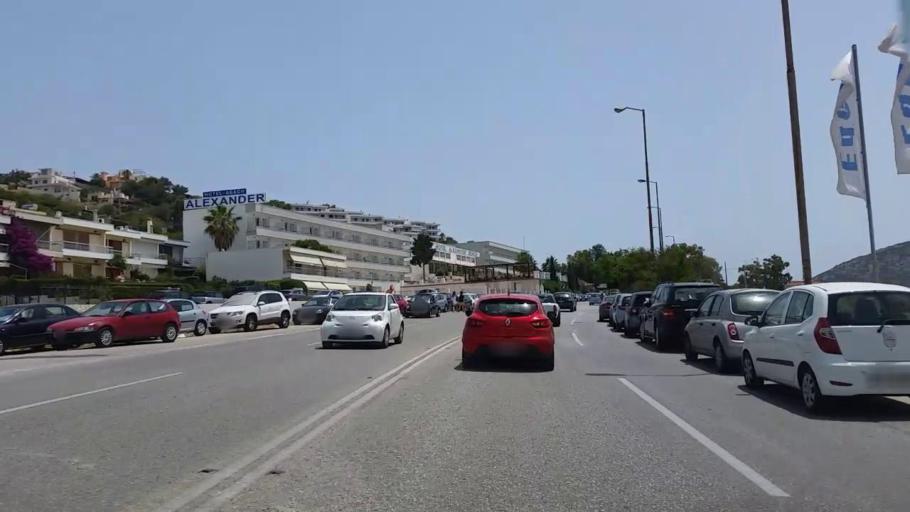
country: GR
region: Attica
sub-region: Nomarchia Anatolikis Attikis
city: Saronida
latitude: 37.7272
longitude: 23.9081
